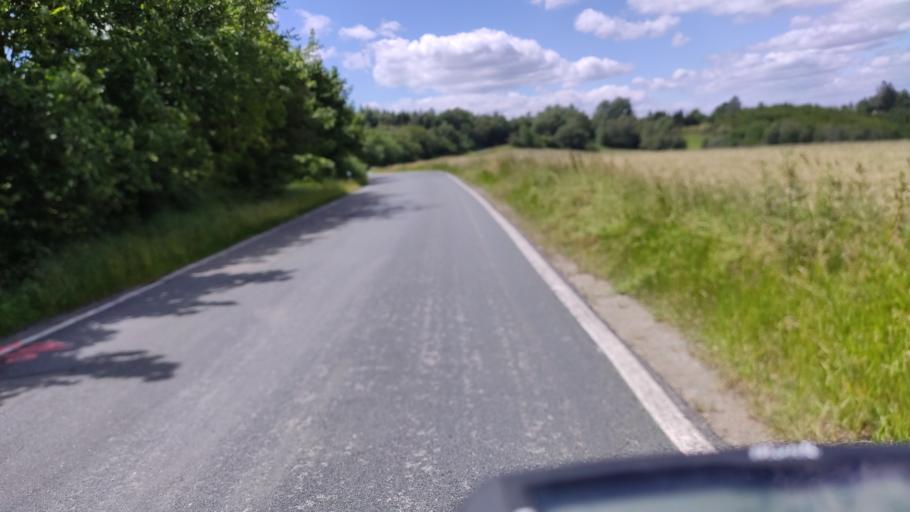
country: DE
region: Thuringia
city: Wurzbach
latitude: 50.4750
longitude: 11.5865
